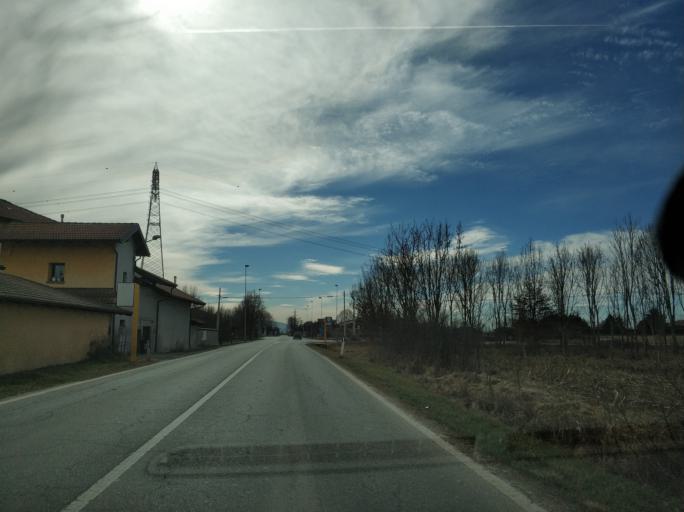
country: IT
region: Piedmont
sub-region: Provincia di Torino
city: Lombardore
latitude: 45.2155
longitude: 7.7303
